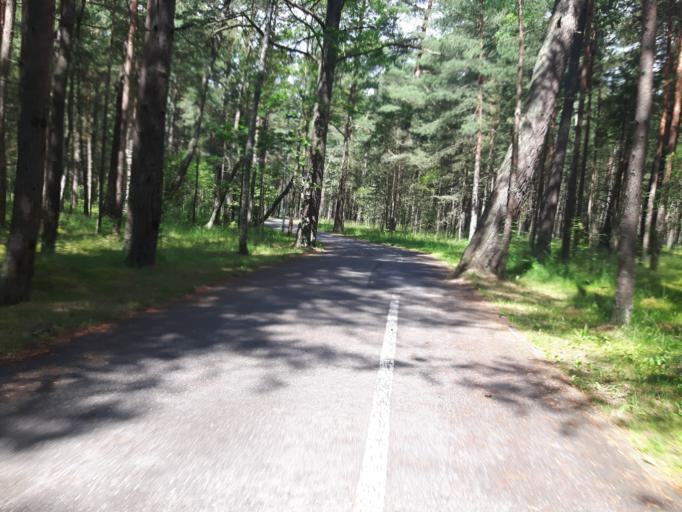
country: LT
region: Klaipedos apskritis
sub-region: Klaipeda
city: Klaipeda
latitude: 55.7600
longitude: 21.1010
